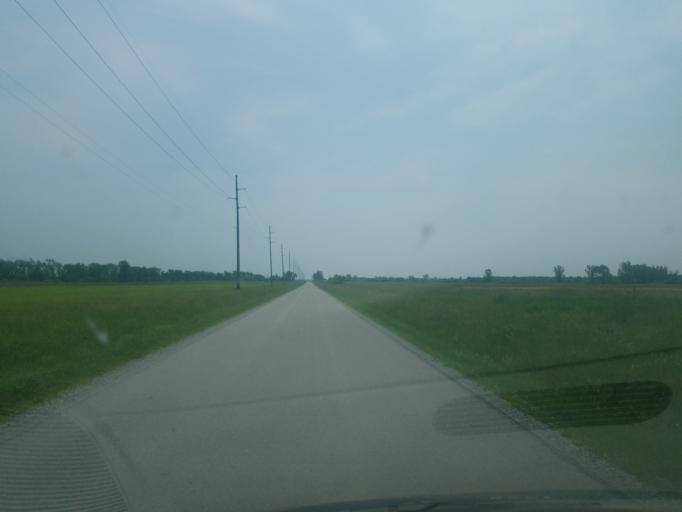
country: US
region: Ohio
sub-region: Wyandot County
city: Upper Sandusky
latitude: 40.7141
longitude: -83.2995
